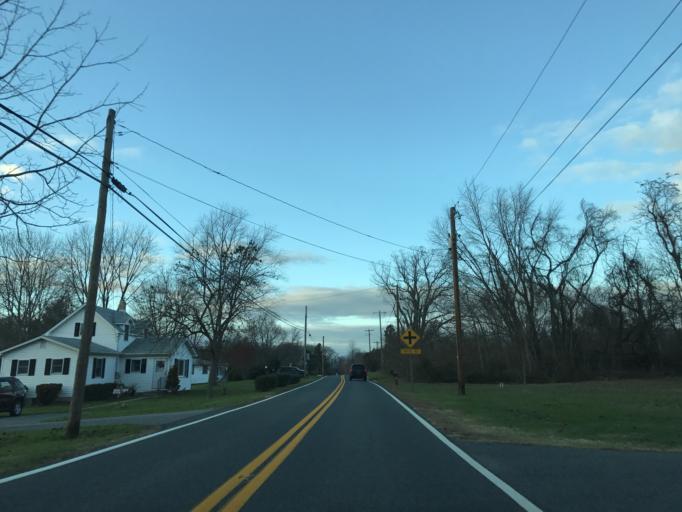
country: US
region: Maryland
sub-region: Cecil County
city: Rising Sun
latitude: 39.6663
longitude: -76.2107
